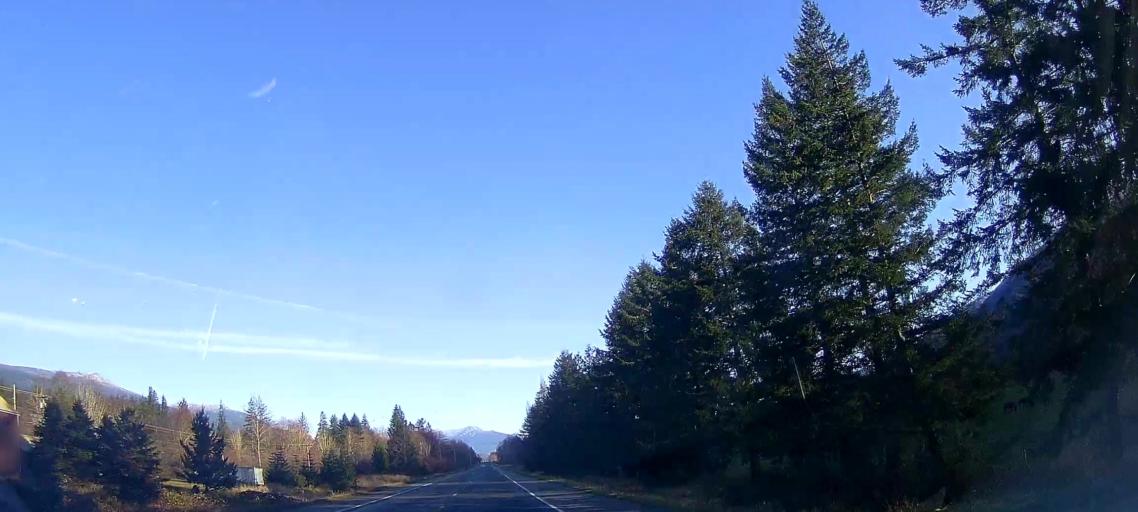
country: US
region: Washington
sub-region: Skagit County
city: Sedro-Woolley
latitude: 48.5236
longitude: -121.9559
